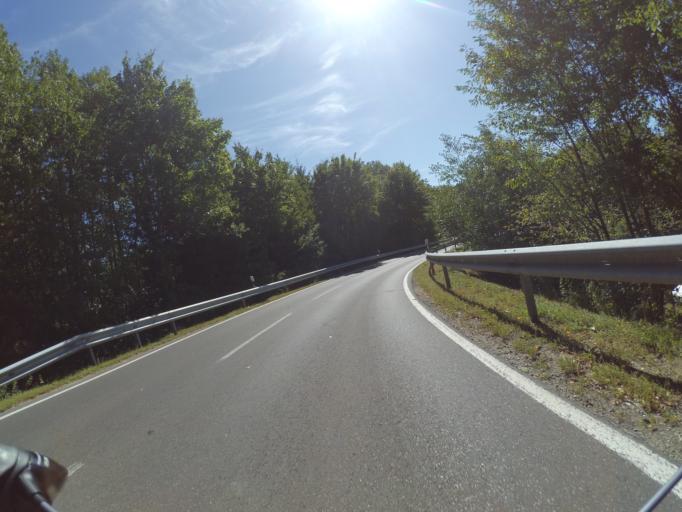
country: DE
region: Rheinland-Pfalz
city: Morbach
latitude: 49.7868
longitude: 7.1064
